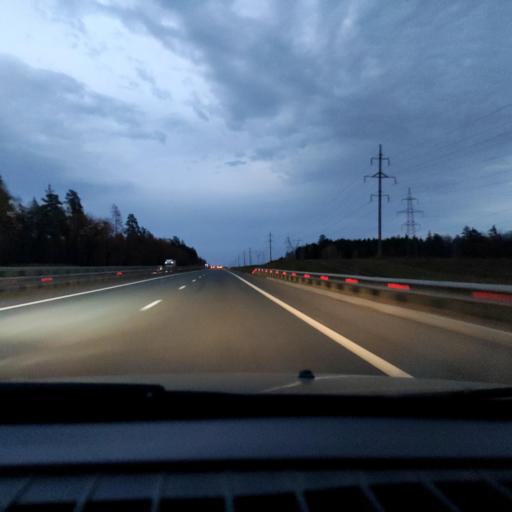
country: RU
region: Samara
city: Povolzhskiy
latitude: 53.5175
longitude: 49.7719
